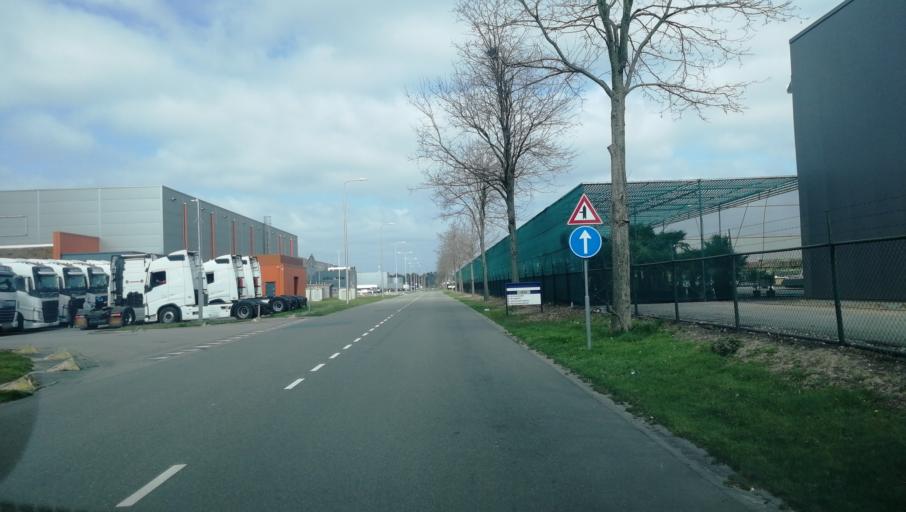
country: NL
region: Limburg
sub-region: Gemeente Venlo
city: Venlo
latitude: 51.4098
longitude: 6.1340
